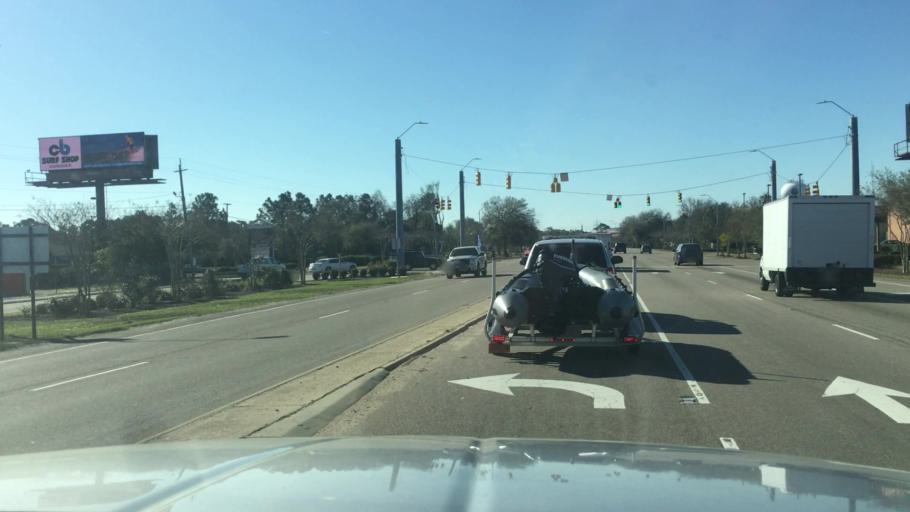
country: US
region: North Carolina
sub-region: New Hanover County
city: Sea Breeze
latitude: 34.0515
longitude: -77.8999
